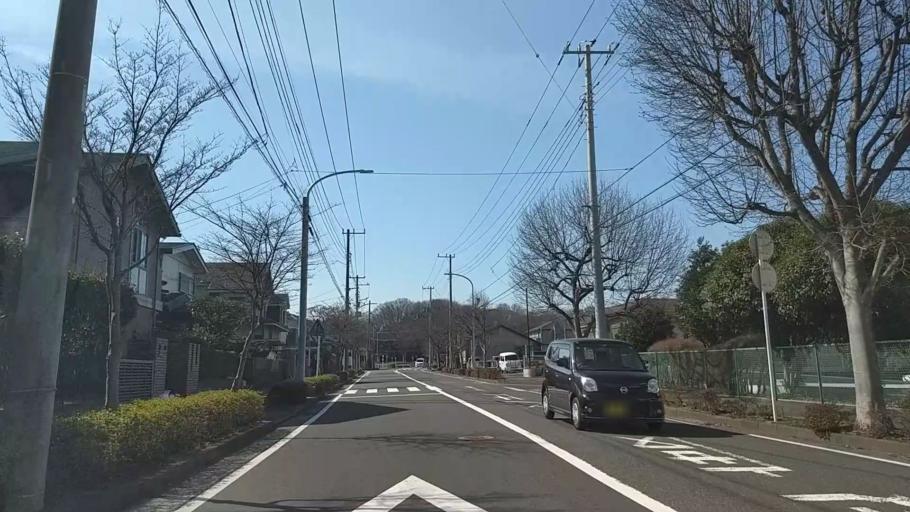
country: JP
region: Kanagawa
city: Kamakura
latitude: 35.3888
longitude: 139.5551
